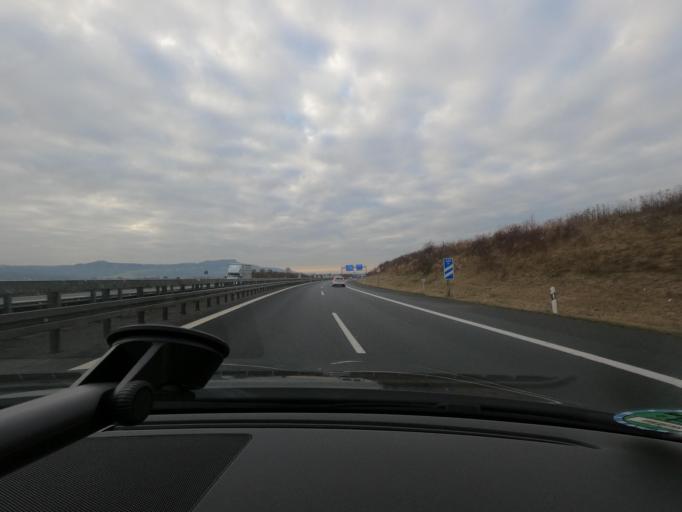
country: DE
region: Bavaria
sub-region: Upper Franconia
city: Lichtenfels
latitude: 50.1291
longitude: 11.0340
